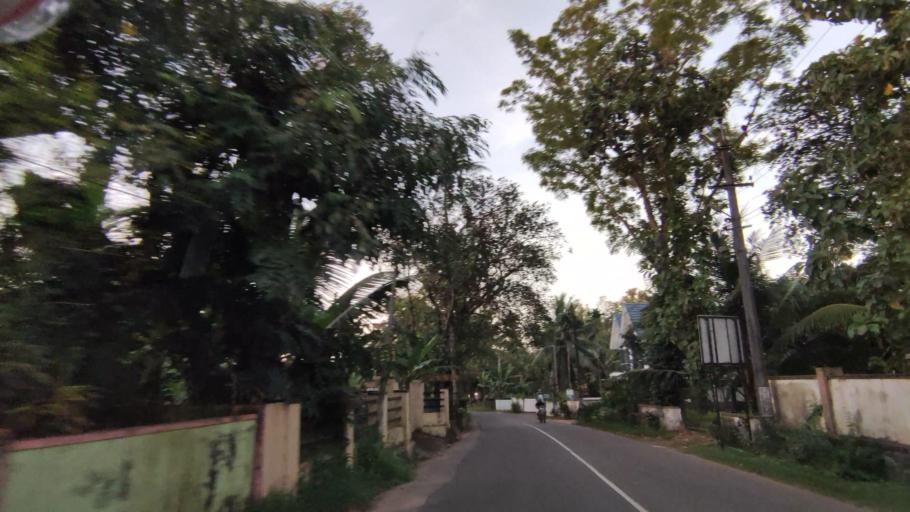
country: IN
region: Kerala
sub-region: Kottayam
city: Kottayam
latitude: 9.6439
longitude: 76.5093
